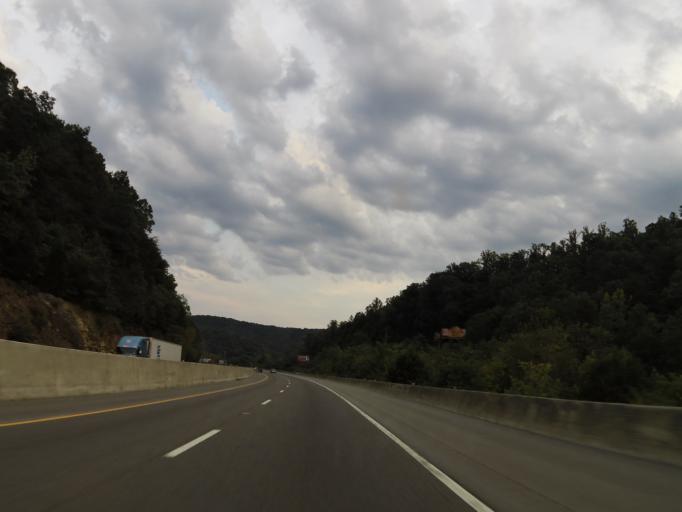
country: US
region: Tennessee
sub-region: Anderson County
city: Norris
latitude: 36.0997
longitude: -84.0214
